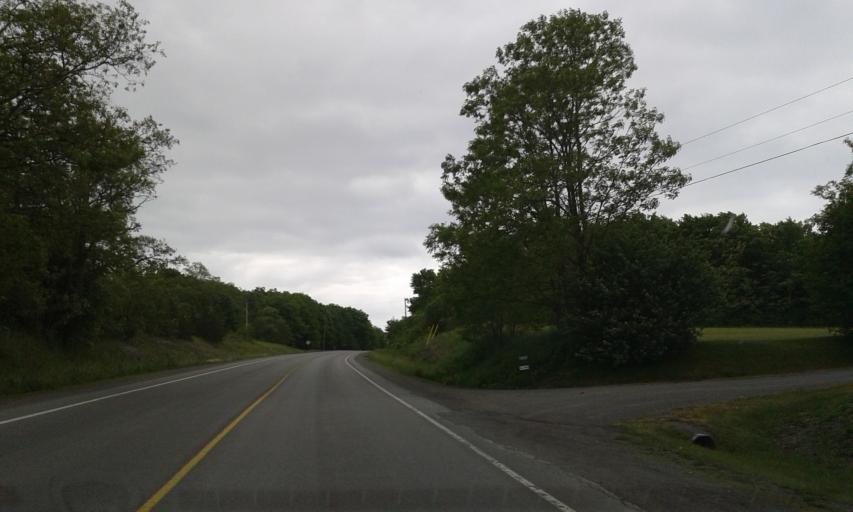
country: CA
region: Ontario
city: Quinte West
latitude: 43.9760
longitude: -77.5064
